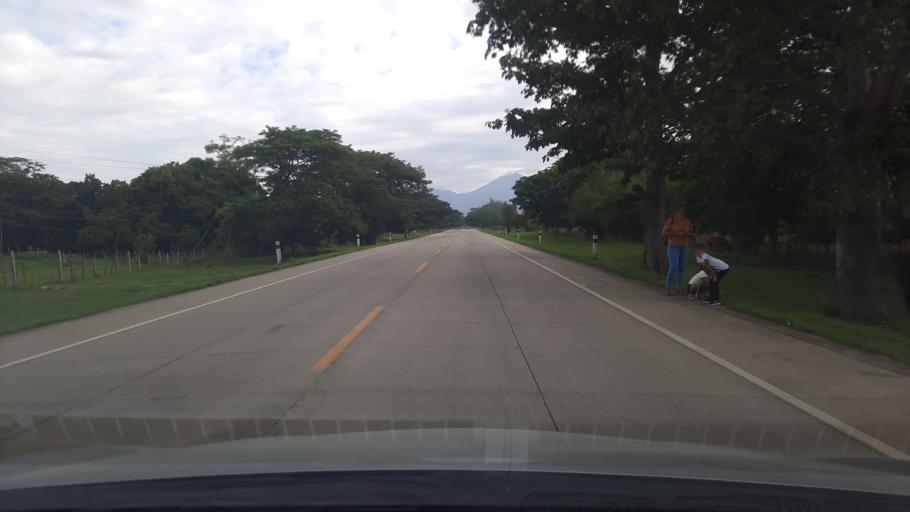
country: NI
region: Chinandega
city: Somotillo
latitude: 12.8565
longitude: -86.8704
